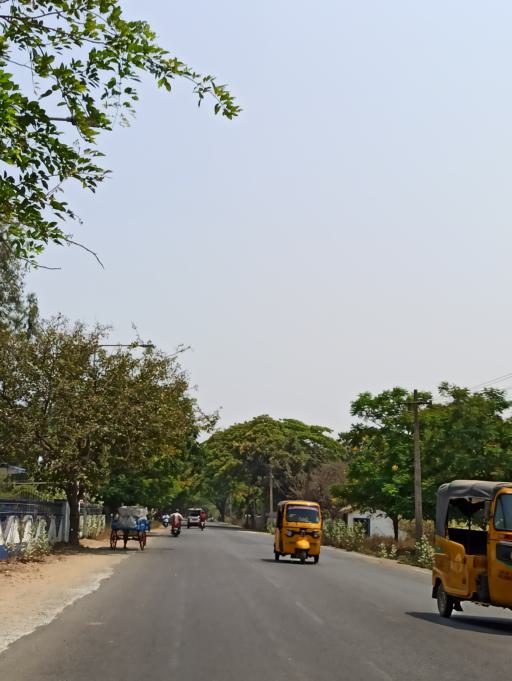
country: IN
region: Tamil Nadu
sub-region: Thiruvallur
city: Chinnasekkadu
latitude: 13.1598
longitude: 80.2439
